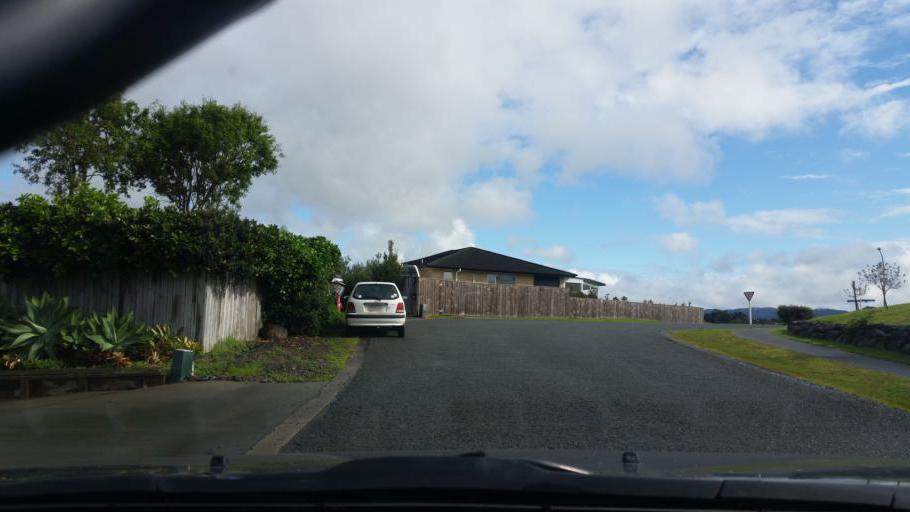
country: NZ
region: Auckland
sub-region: Auckland
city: Wellsford
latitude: -36.0873
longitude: 174.5776
